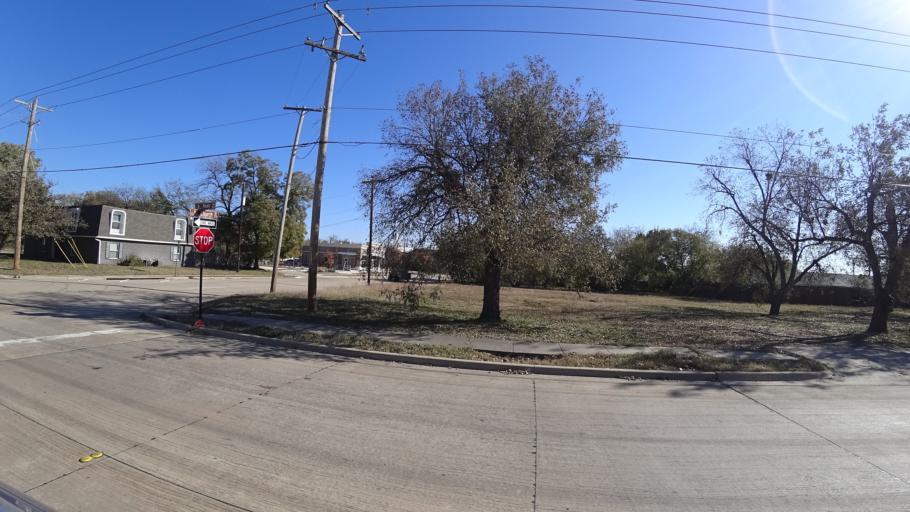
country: US
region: Texas
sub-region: Denton County
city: Lewisville
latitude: 33.0471
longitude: -96.9928
